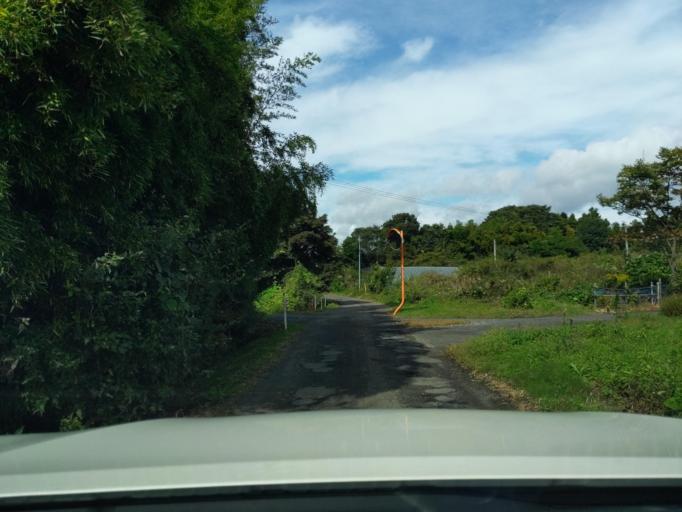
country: JP
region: Fukushima
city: Koriyama
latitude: 37.4027
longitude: 140.3178
